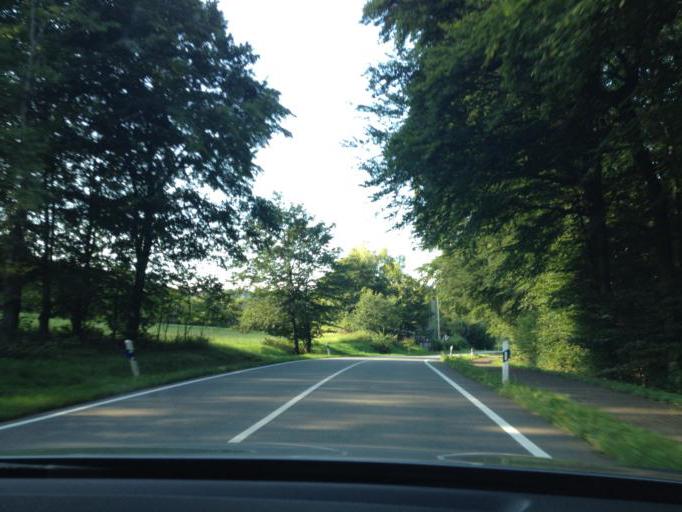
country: DE
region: Saarland
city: Tholey
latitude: 49.4840
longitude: 6.9736
